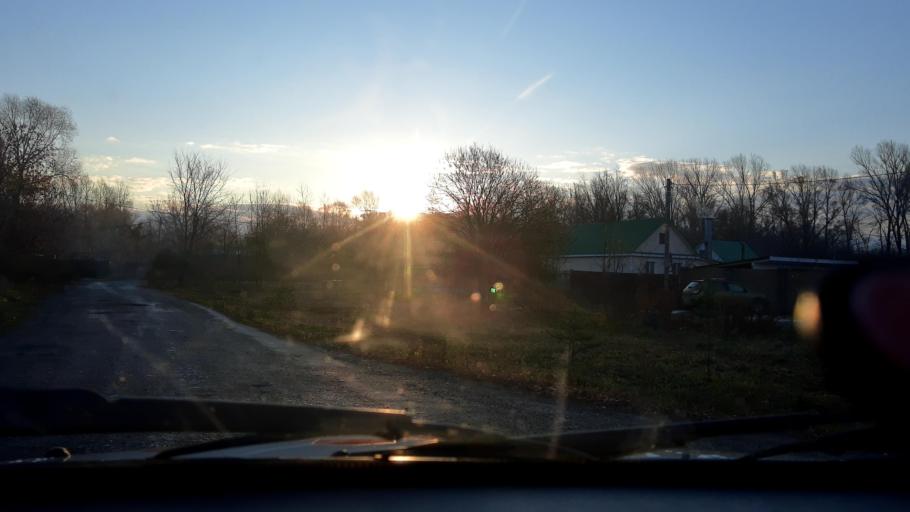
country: RU
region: Bashkortostan
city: Ufa
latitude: 54.8002
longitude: 56.1662
